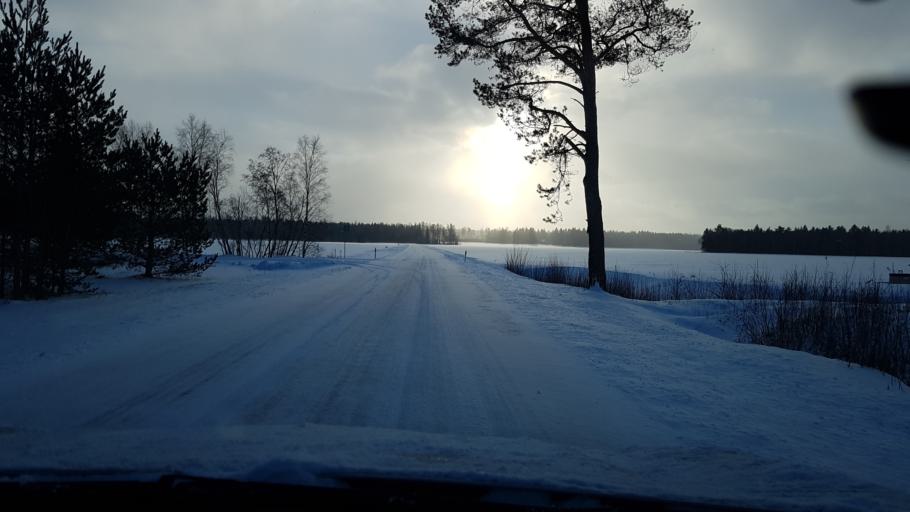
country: EE
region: Harju
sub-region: Nissi vald
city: Turba
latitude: 59.2057
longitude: 24.1406
